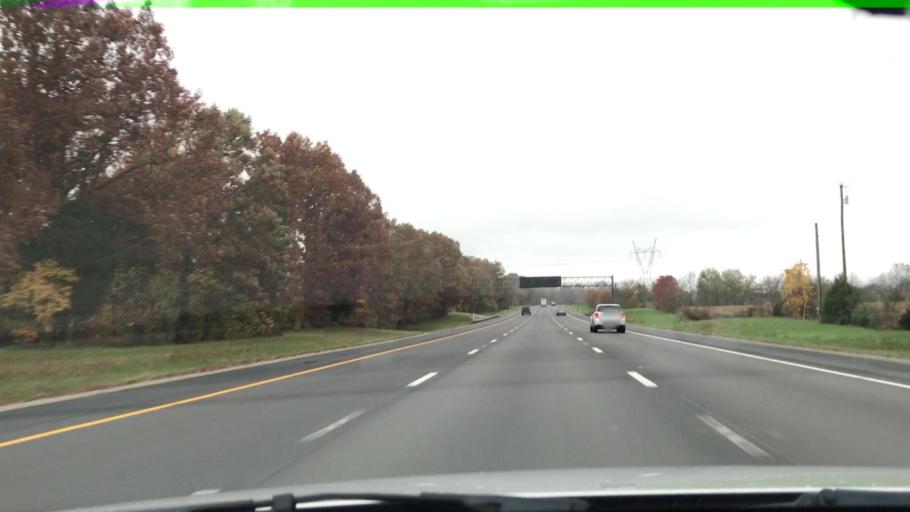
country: US
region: Kentucky
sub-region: Warren County
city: Bowling Green
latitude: 37.0148
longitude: -86.2841
